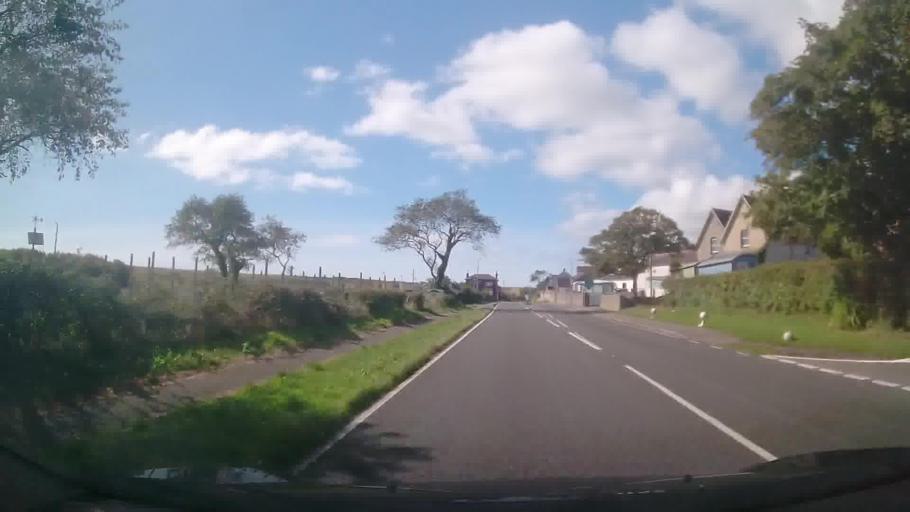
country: GB
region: Wales
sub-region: Pembrokeshire
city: Penally
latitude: 51.6599
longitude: -4.7212
